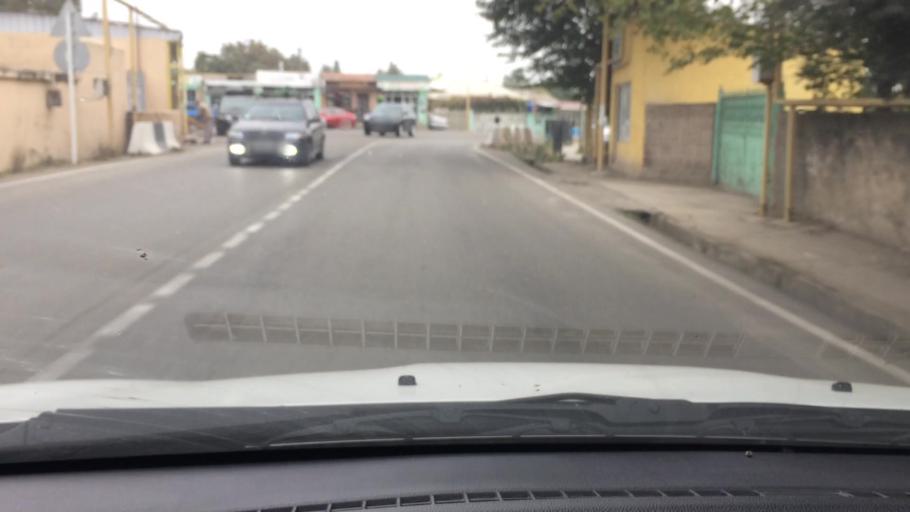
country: AM
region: Tavush
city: Bagratashen
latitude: 41.2448
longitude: 44.7978
